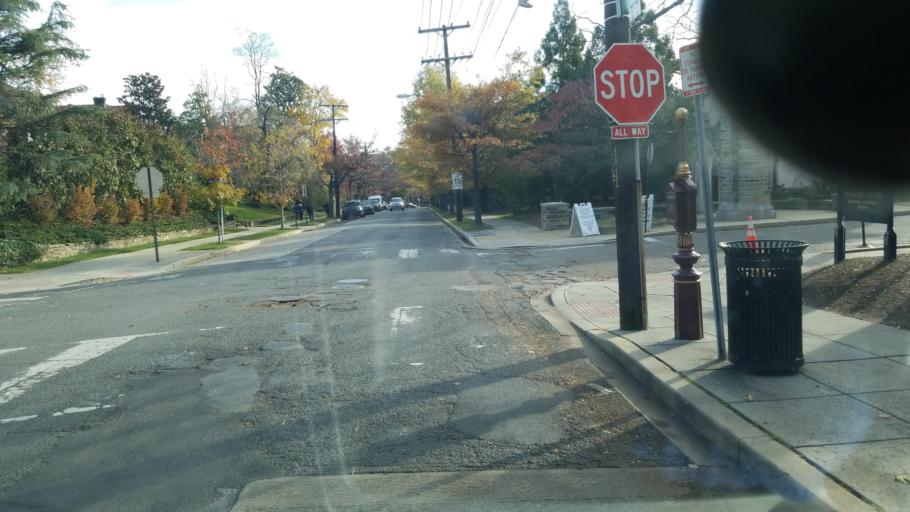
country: US
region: Maryland
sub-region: Montgomery County
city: Friendship Village
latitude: 38.9316
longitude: -77.0688
